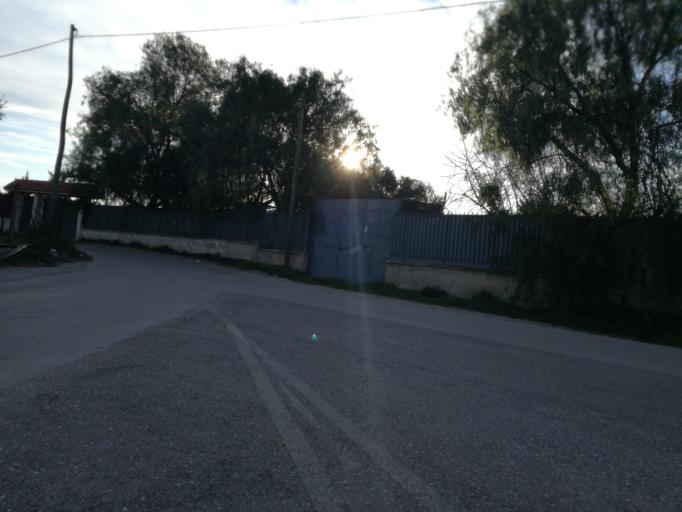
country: IT
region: Apulia
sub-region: Provincia di Bari
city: Valenzano
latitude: 41.0535
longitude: 16.8955
